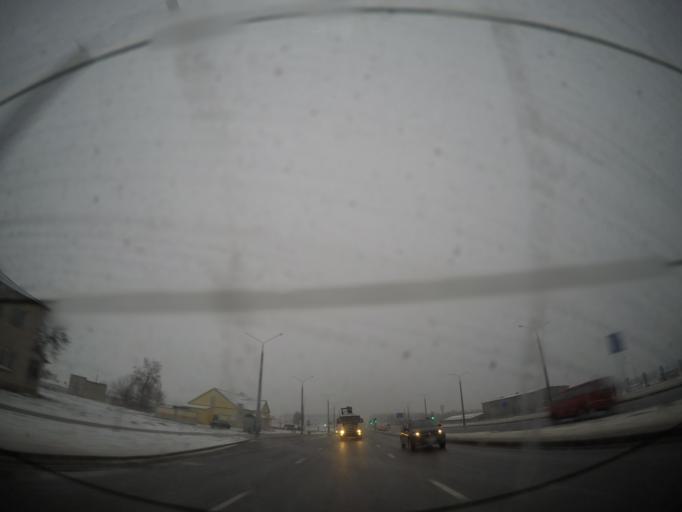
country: BY
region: Grodnenskaya
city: Hrodna
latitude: 53.6399
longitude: 23.8157
